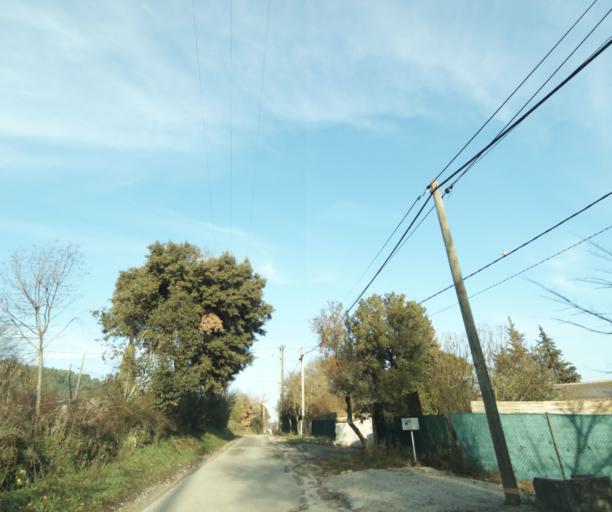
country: FR
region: Provence-Alpes-Cote d'Azur
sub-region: Departement du Var
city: Tourves
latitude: 43.3992
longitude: 5.9308
